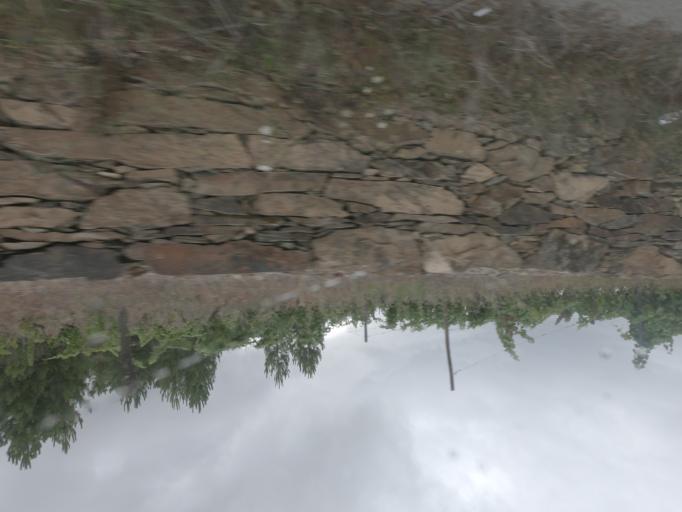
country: PT
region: Vila Real
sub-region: Sabrosa
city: Sabrosa
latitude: 41.2357
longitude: -7.4953
